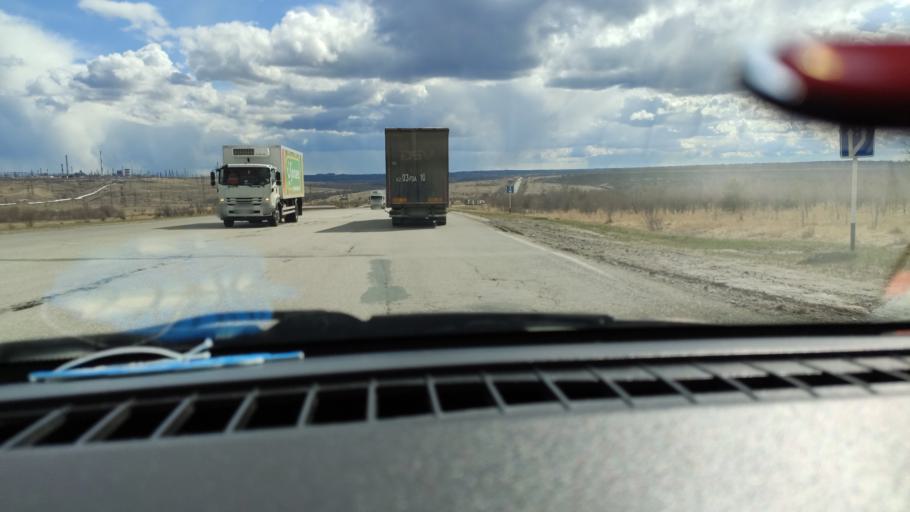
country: RU
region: Samara
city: Varlamovo
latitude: 53.1034
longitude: 48.3570
